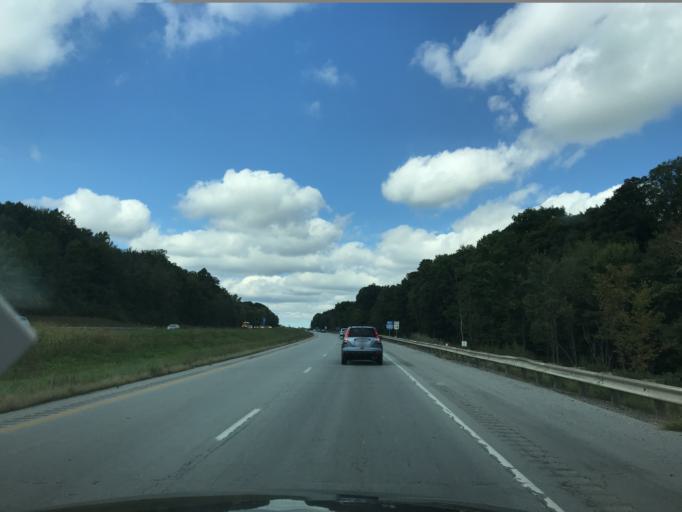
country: US
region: Ohio
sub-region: Summit County
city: Twinsburg
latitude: 41.3162
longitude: -81.4562
